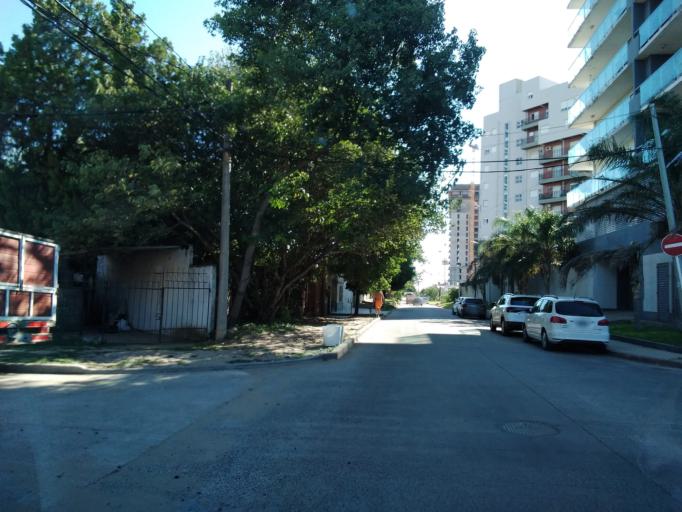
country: AR
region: Corrientes
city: Corrientes
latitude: -27.4759
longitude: -58.8525
